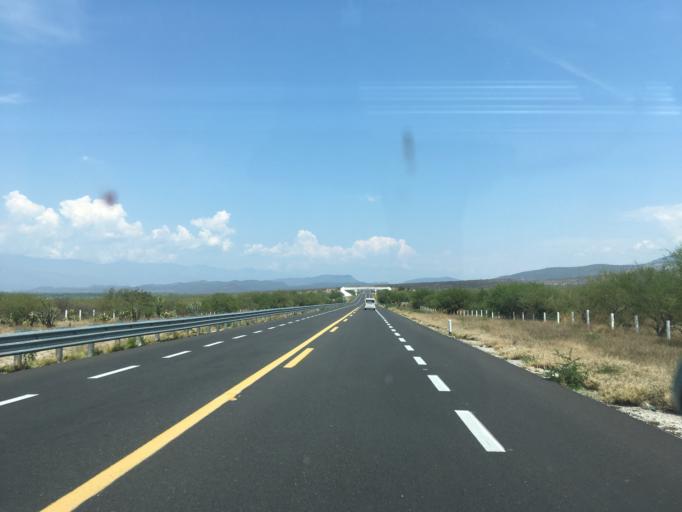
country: MX
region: Puebla
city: San Gabriel Chilac
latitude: 18.2909
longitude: -97.3424
